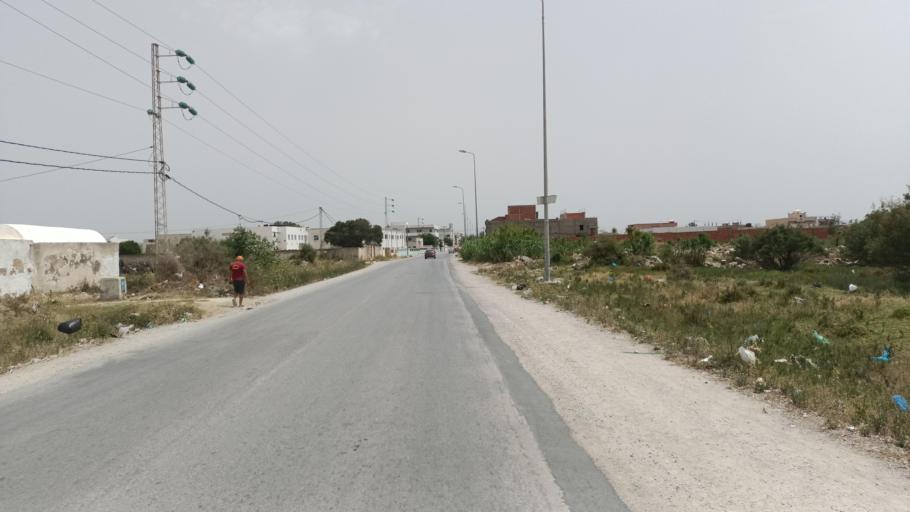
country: TN
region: Nabul
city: Manzil Bu Zalafah
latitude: 36.7091
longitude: 10.4836
